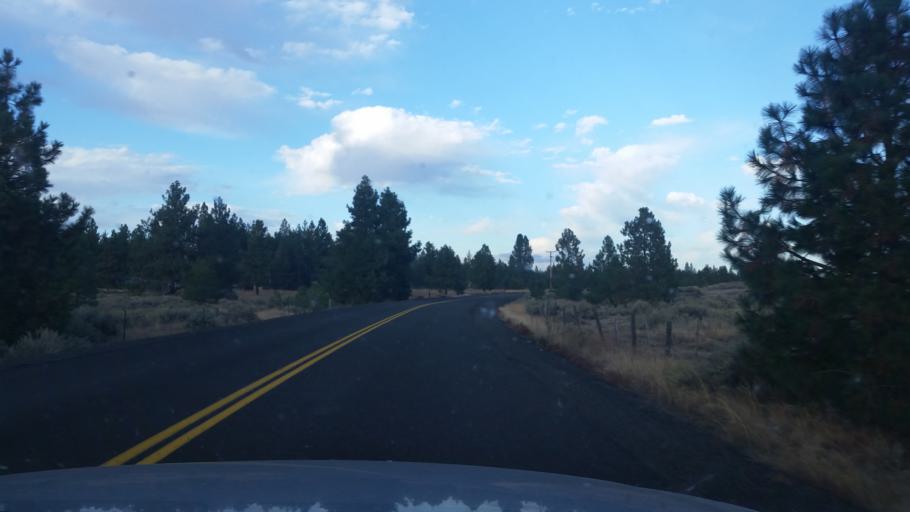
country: US
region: Washington
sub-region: Spokane County
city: Medical Lake
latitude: 47.4519
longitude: -117.8163
